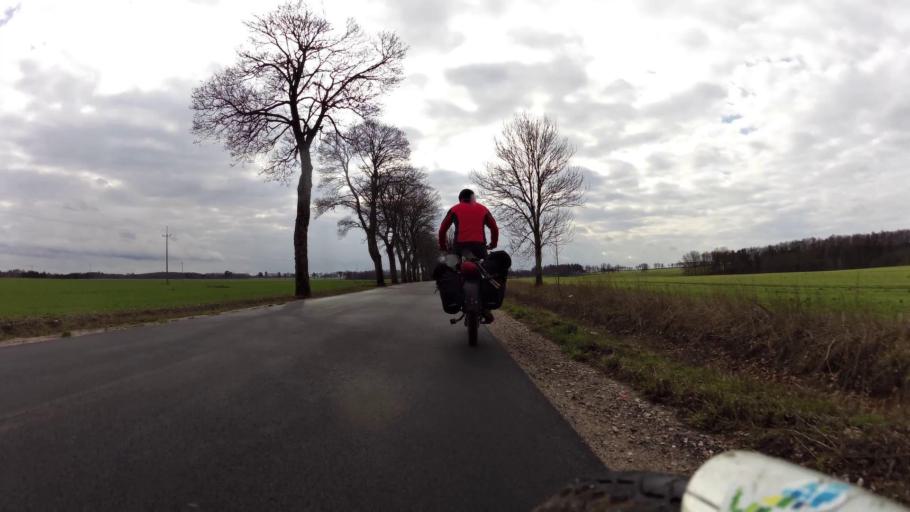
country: PL
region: Pomeranian Voivodeship
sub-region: Powiat bytowski
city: Kolczyglowy
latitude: 54.2329
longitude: 17.2423
